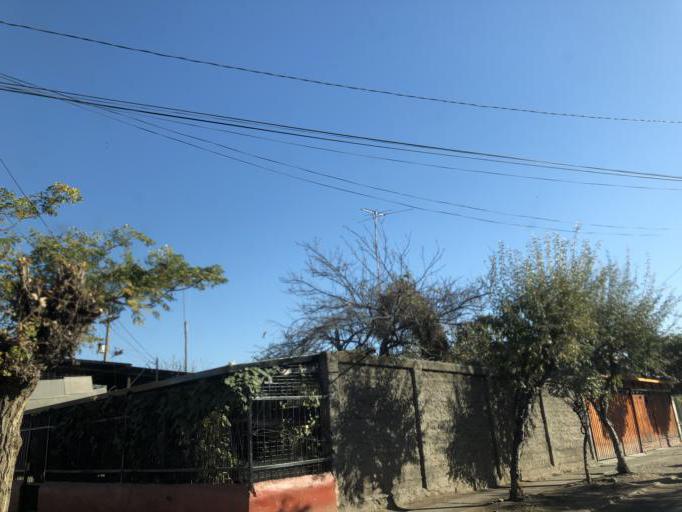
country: CL
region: Santiago Metropolitan
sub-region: Provincia de Cordillera
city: Puente Alto
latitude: -33.6174
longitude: -70.5939
